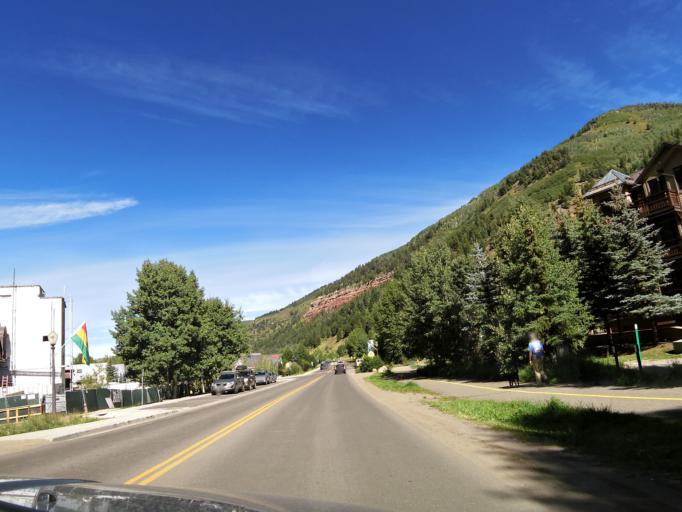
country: US
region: Colorado
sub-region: San Miguel County
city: Telluride
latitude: 37.9395
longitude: -107.8187
